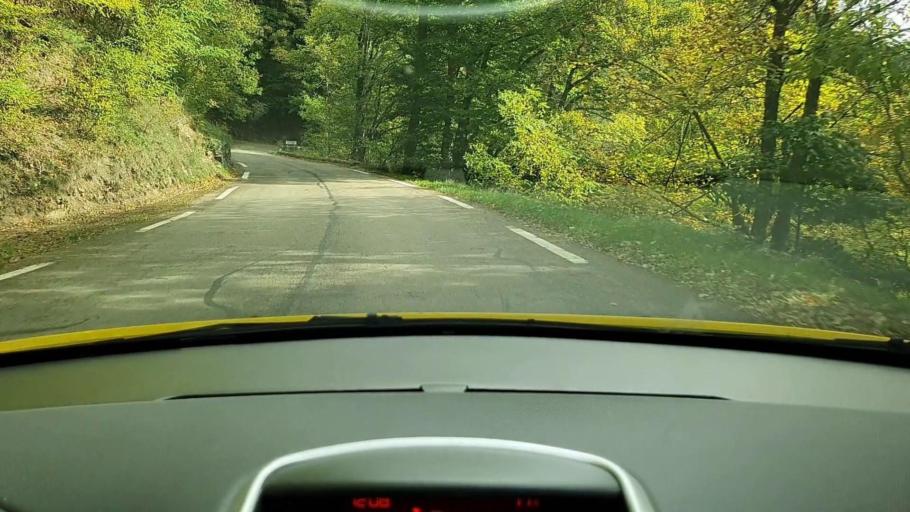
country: FR
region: Languedoc-Roussillon
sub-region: Departement de la Lozere
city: Meyrueis
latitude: 44.1239
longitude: 3.4744
